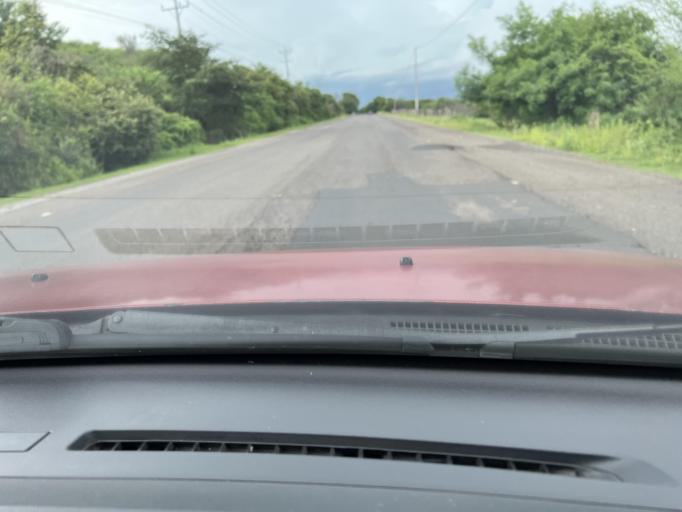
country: SV
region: La Union
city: San Alejo
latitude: 13.4007
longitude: -87.8966
